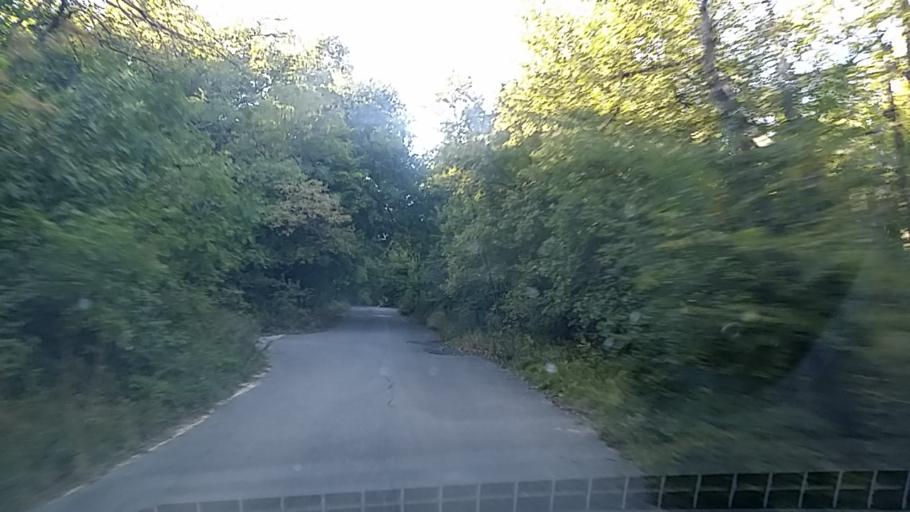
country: HU
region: Budapest
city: Budapest II. keruelet
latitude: 47.5461
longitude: 18.9916
